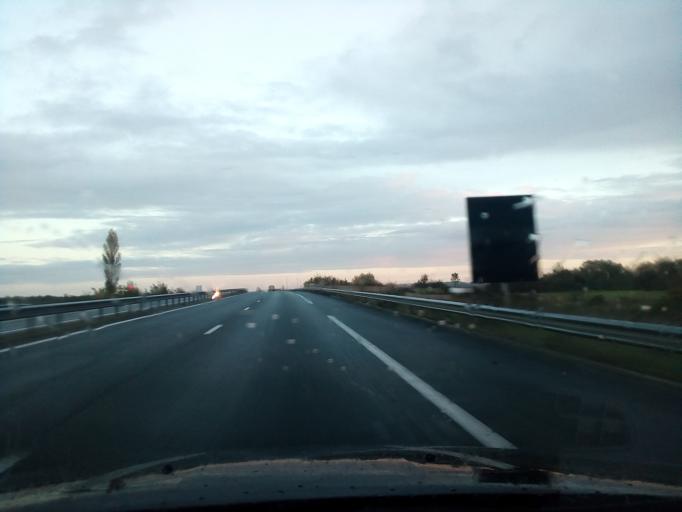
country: FR
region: Aquitaine
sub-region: Departement de la Gironde
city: Cavignac
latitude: 45.0918
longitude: -0.3813
